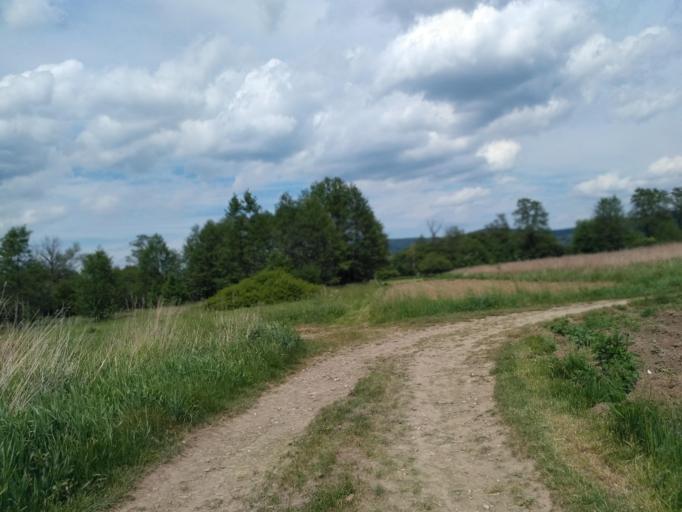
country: PL
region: Subcarpathian Voivodeship
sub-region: Powiat krosnienski
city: Odrzykon
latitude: 49.7193
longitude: 21.7467
